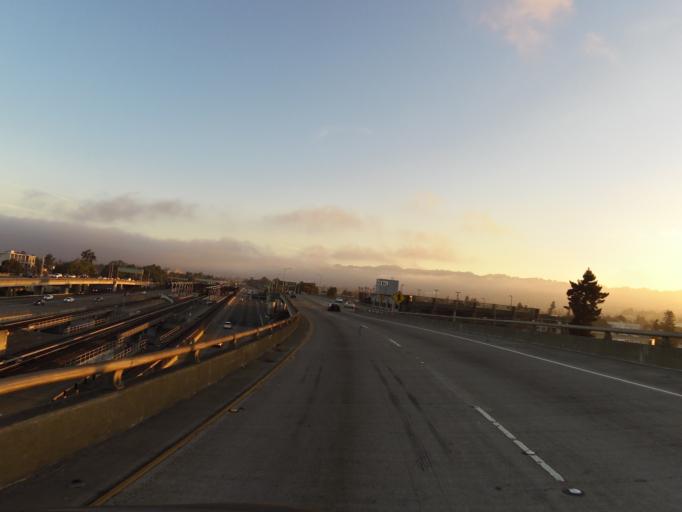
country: US
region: California
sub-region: Alameda County
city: Emeryville
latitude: 37.8256
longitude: -122.2677
